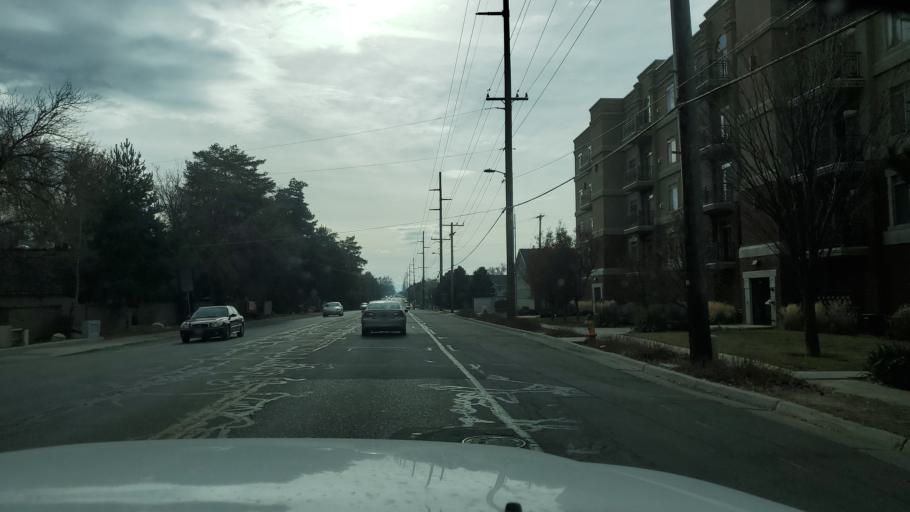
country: US
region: Utah
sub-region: Salt Lake County
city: Millcreek
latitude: 40.6864
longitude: -111.8656
